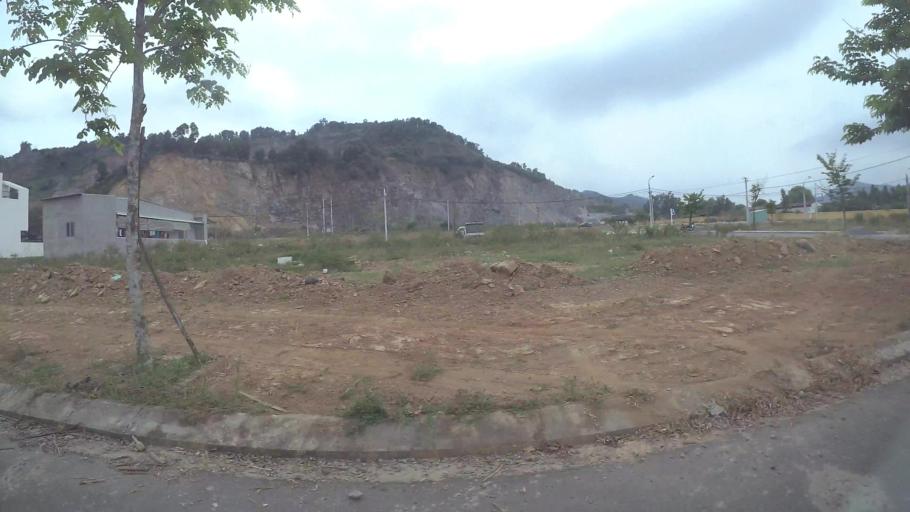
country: VN
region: Da Nang
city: Lien Chieu
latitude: 16.0426
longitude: 108.1670
